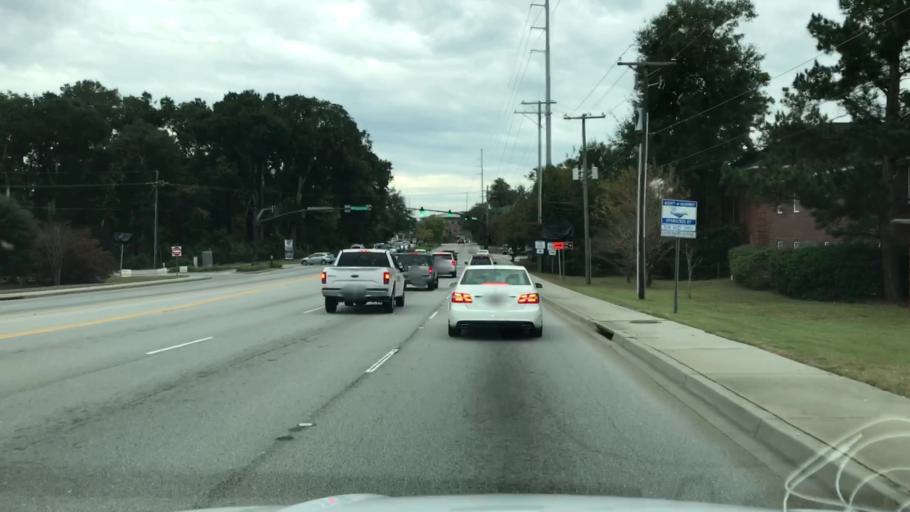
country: US
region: South Carolina
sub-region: Charleston County
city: Charleston
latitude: 32.7644
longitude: -79.9745
